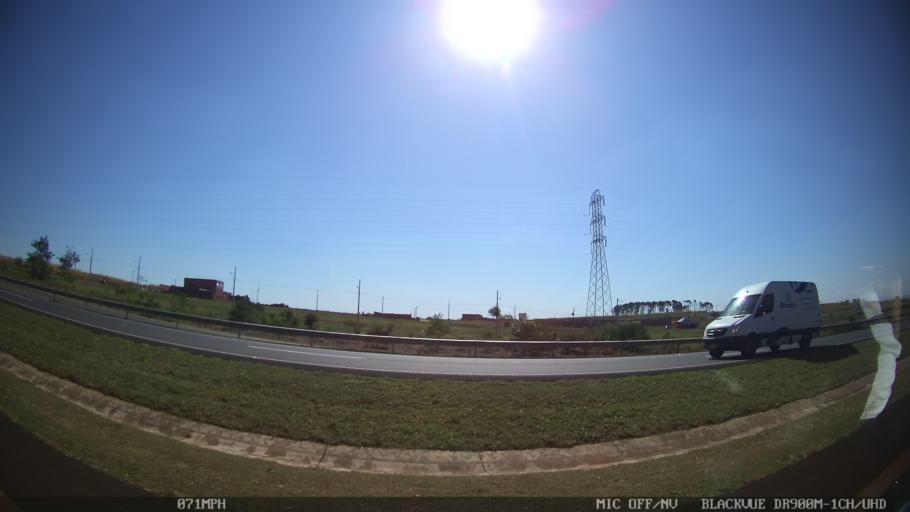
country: BR
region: Sao Paulo
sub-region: Ribeirao Preto
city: Ribeirao Preto
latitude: -21.1276
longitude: -47.8460
